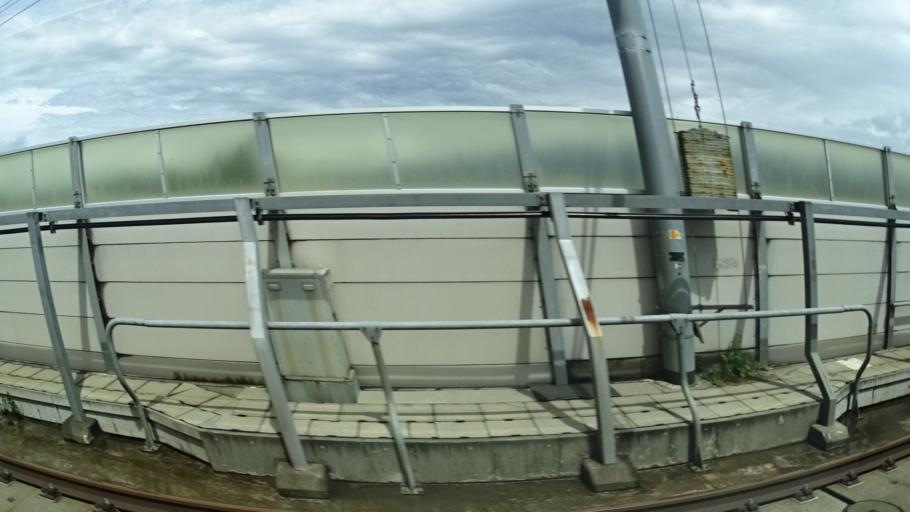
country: JP
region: Nagano
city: Komoro
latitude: 36.2721
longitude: 138.4448
